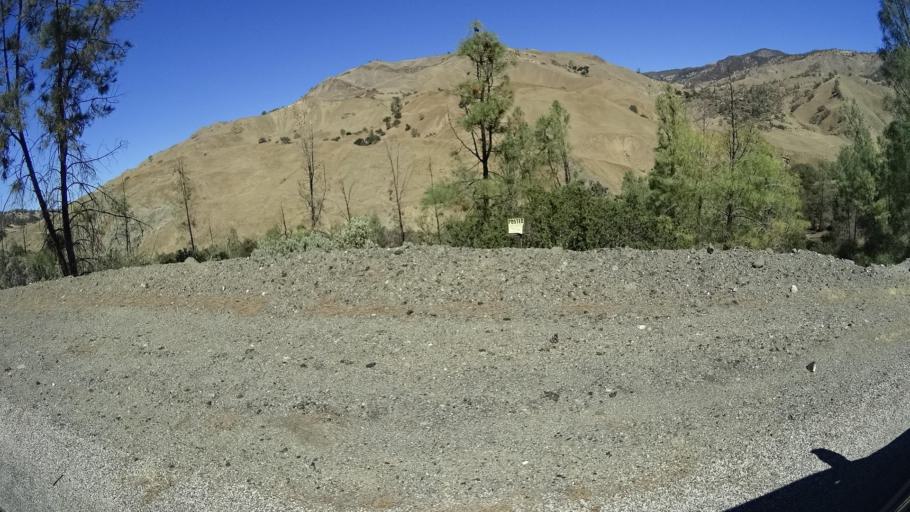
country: US
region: California
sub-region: Monterey County
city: King City
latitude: 36.2915
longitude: -120.8772
